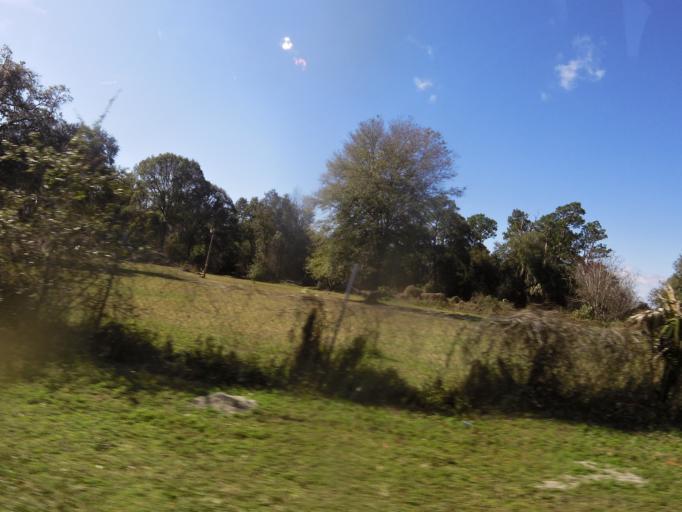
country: US
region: Florida
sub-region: Putnam County
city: Crescent City
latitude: 29.3337
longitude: -81.4972
